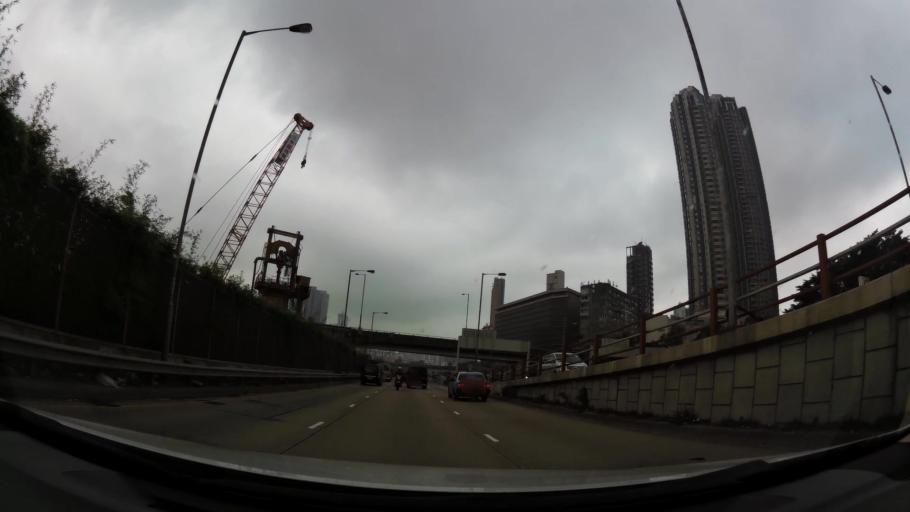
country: HK
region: Kowloon City
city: Kowloon
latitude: 22.3309
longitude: 114.1950
